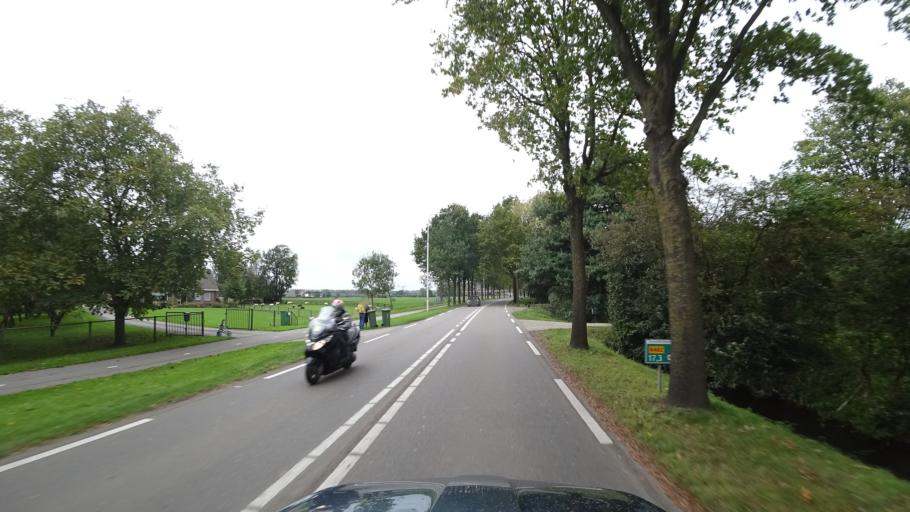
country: NL
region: Utrecht
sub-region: Stichtse Vecht
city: Spechtenkamp
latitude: 52.1518
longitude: 5.0282
